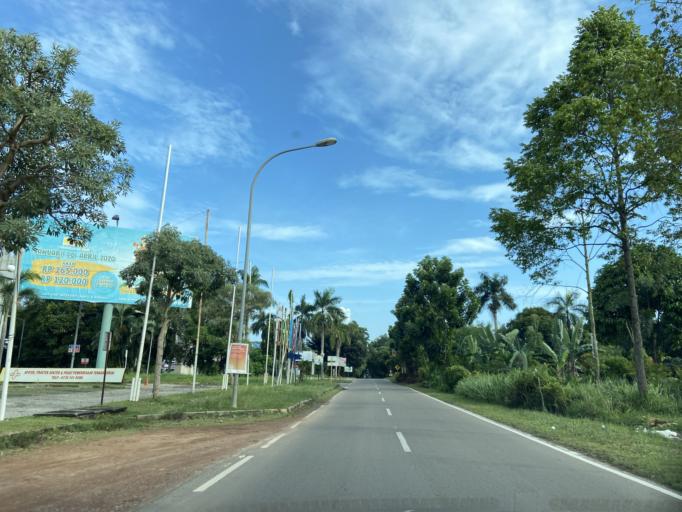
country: SG
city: Singapore
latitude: 1.1071
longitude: 104.0297
